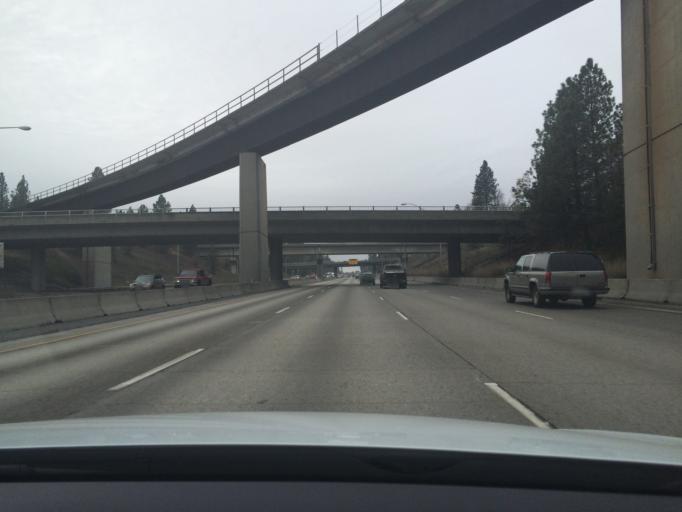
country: US
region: Washington
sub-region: Spokane County
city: Spokane
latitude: 47.6465
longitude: -117.4519
